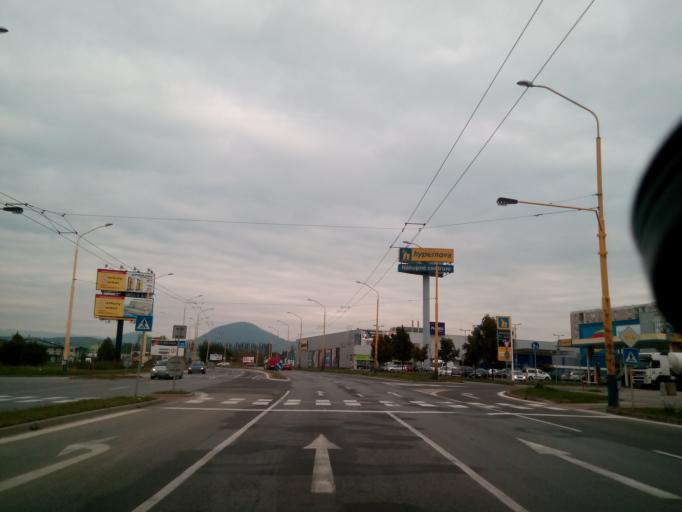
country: SK
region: Presovsky
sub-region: Okres Presov
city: Presov
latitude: 48.9982
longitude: 21.2700
